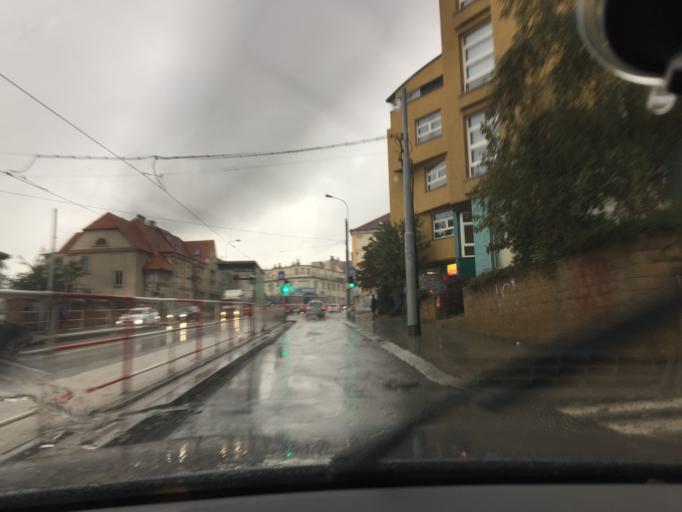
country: CZ
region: Praha
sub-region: Praha 8
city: Liben
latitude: 50.1197
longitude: 14.4606
